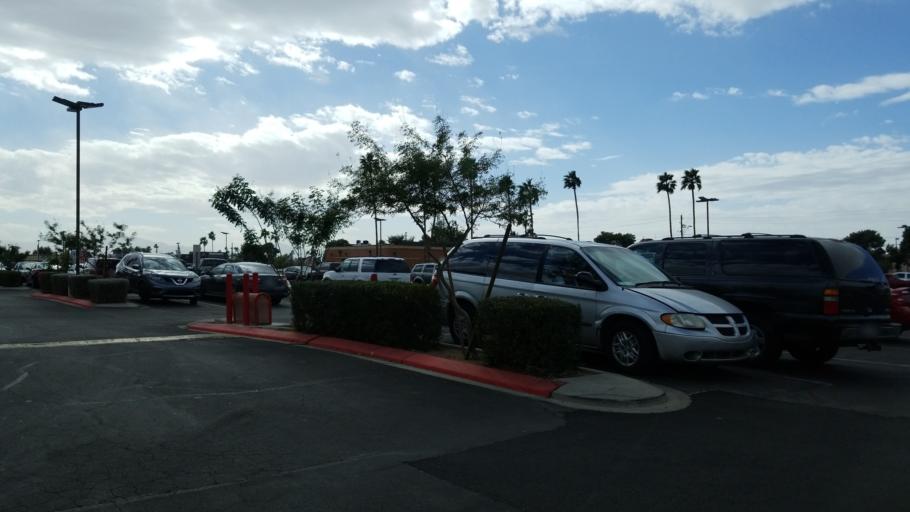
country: US
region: Arizona
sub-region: Maricopa County
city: Tolleson
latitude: 33.4791
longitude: -112.2194
